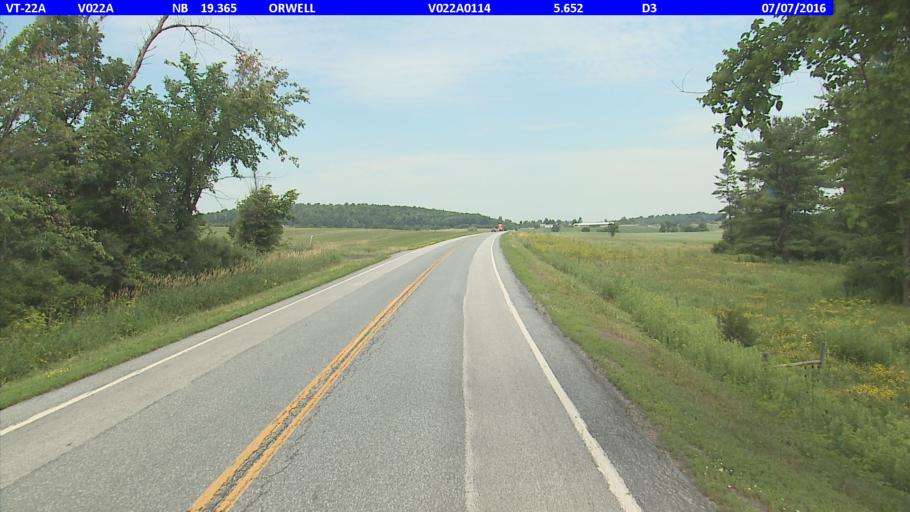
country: US
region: New York
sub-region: Essex County
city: Ticonderoga
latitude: 43.8382
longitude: -73.3099
